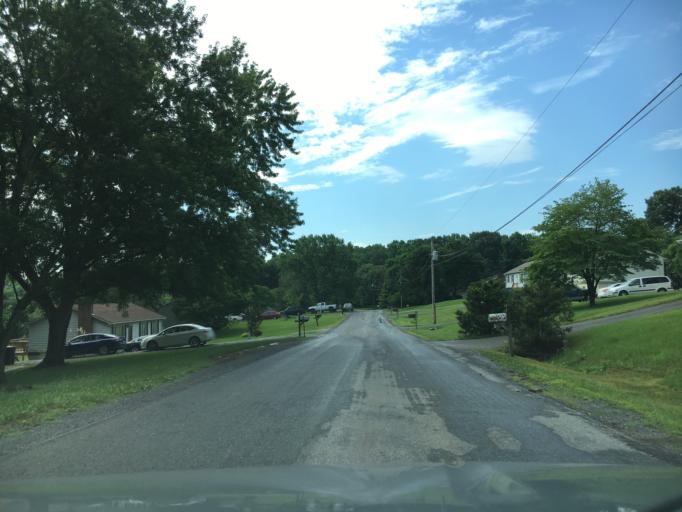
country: US
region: Virginia
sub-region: Bedford County
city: Forest
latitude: 37.3613
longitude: -79.2643
